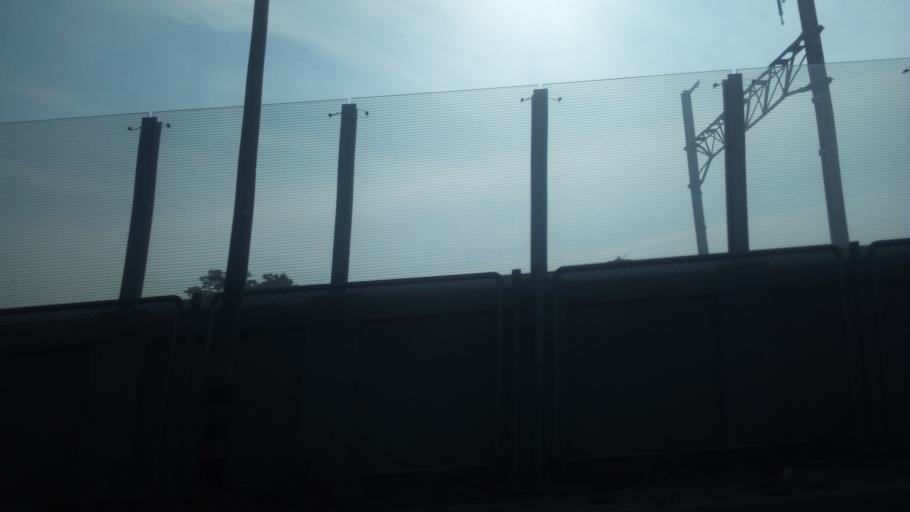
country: TH
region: Phra Nakhon Si Ayutthaya
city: Ban Bang Kadi Pathum Thani
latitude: 13.9742
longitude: 100.6039
